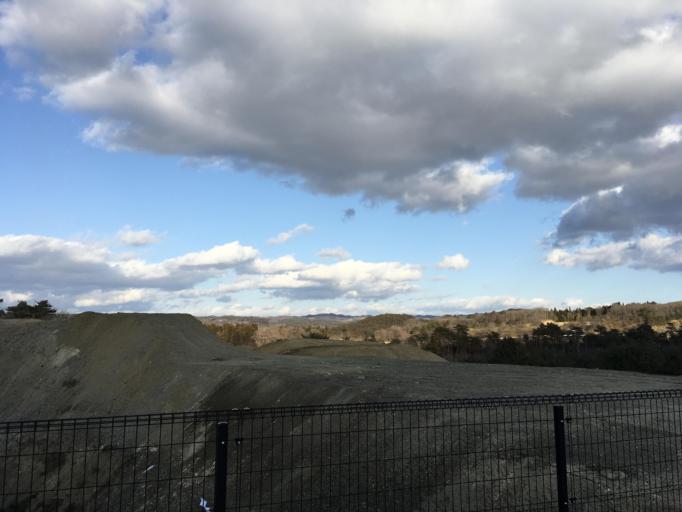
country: JP
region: Iwate
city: Ichinoseki
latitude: 38.7801
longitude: 141.2277
